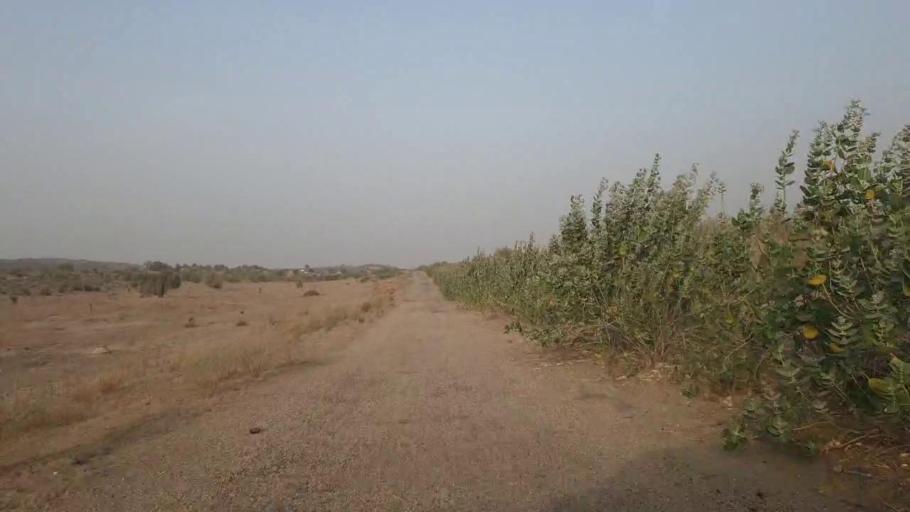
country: PK
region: Sindh
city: Chor
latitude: 25.4843
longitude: 69.9072
